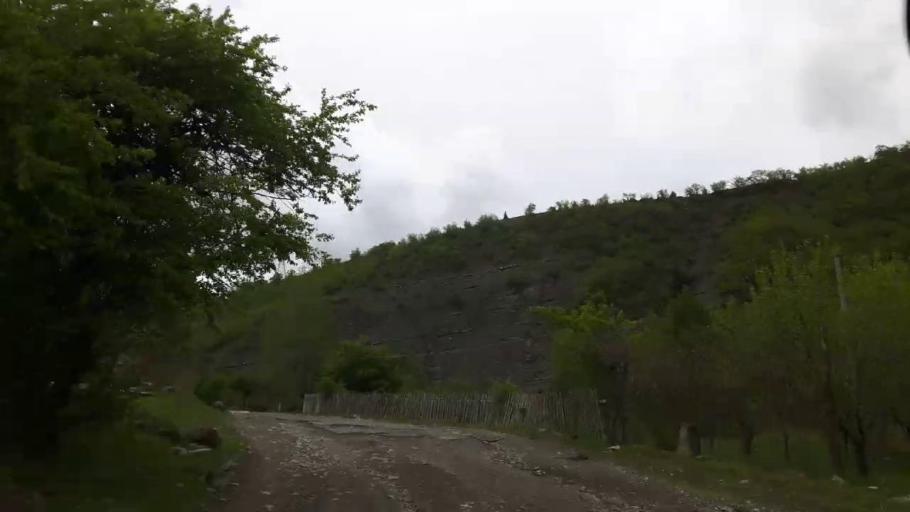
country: GE
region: Shida Kartli
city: Gori
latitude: 41.8688
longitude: 43.9834
